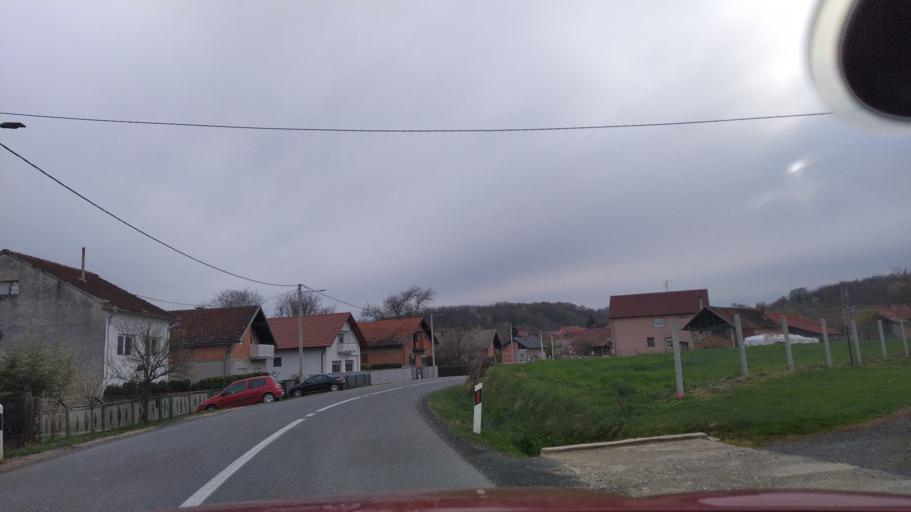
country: HR
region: Varazdinska
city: Ludbreg
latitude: 46.2377
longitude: 16.5497
